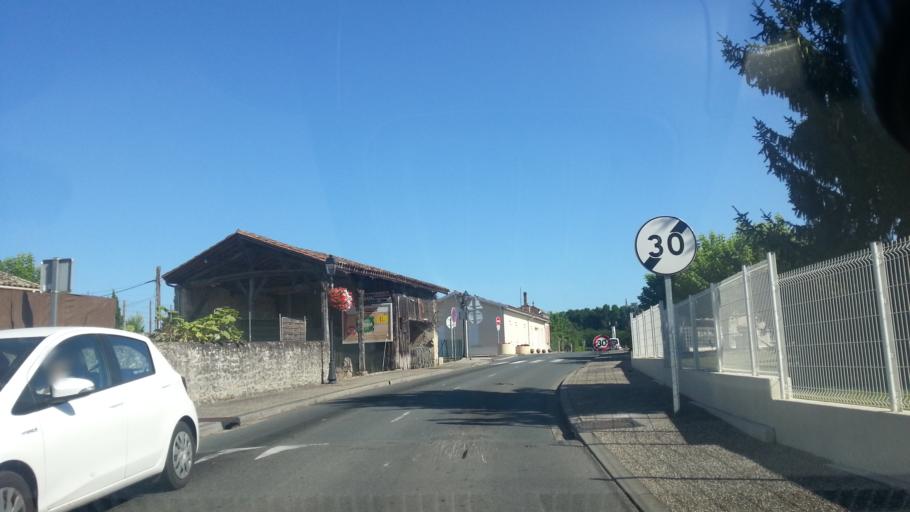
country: FR
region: Aquitaine
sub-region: Departement de la Gironde
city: Illats
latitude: 44.6002
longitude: -0.3701
